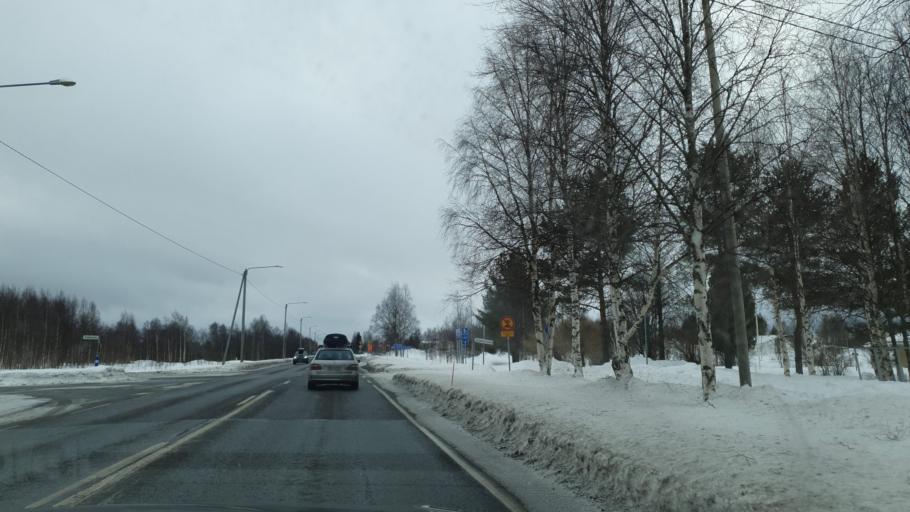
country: FI
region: Lapland
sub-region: Kemi-Tornio
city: Tornio
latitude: 65.9190
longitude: 24.1347
